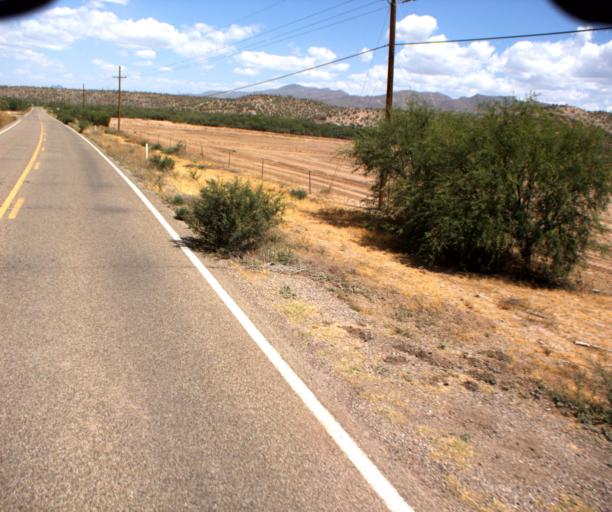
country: US
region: Arizona
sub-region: Pinal County
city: Kearny
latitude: 33.0427
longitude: -110.8839
